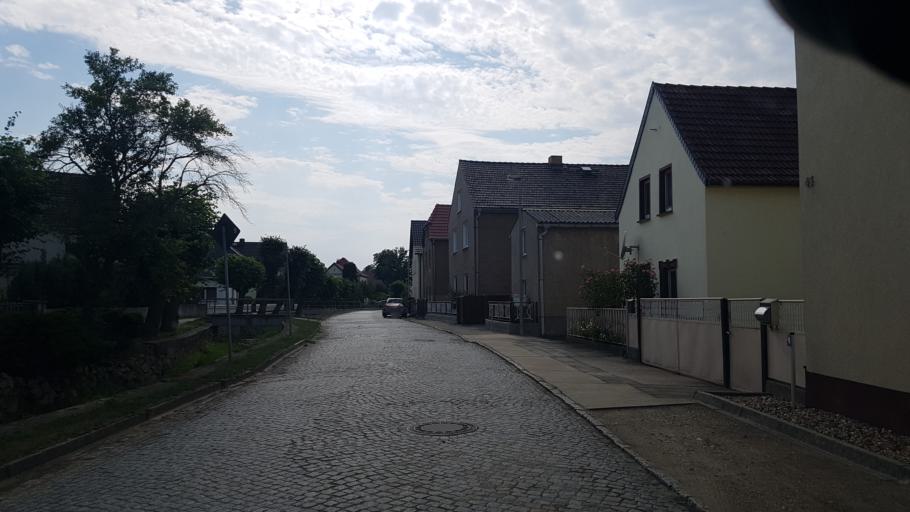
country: DE
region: Brandenburg
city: Grossthiemig
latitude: 51.3865
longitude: 13.6840
